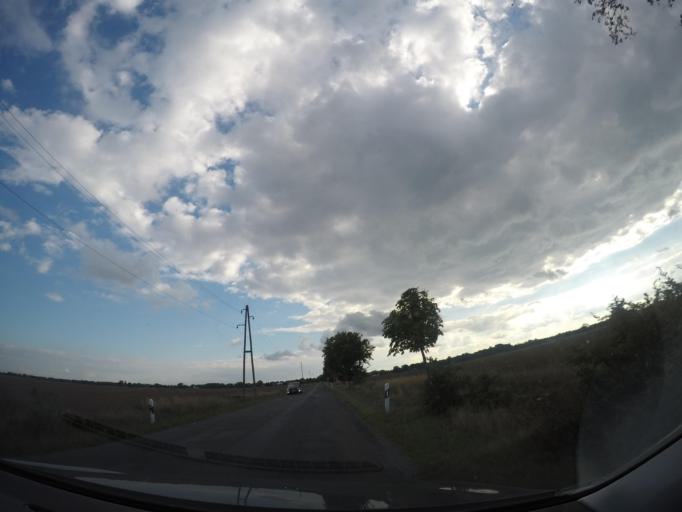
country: DE
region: Saxony-Anhalt
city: Mieste
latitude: 52.5154
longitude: 11.1461
